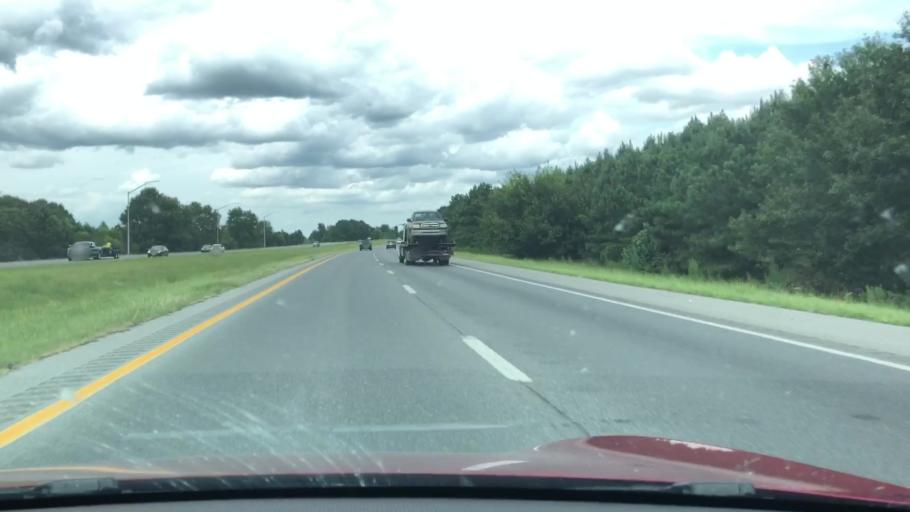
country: US
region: Maryland
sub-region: Wicomico County
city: Salisbury
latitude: 38.3293
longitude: -75.5751
